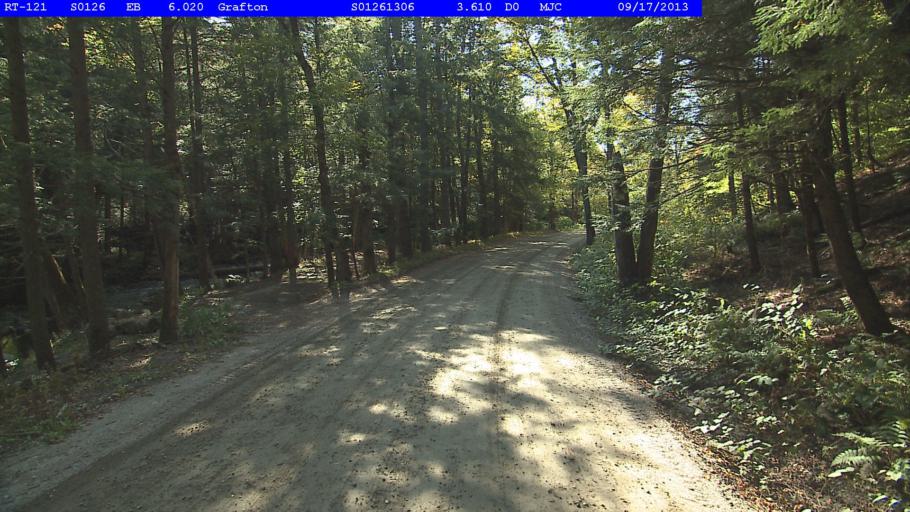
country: US
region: Vermont
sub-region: Windsor County
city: Chester
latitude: 43.1970
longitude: -72.6196
